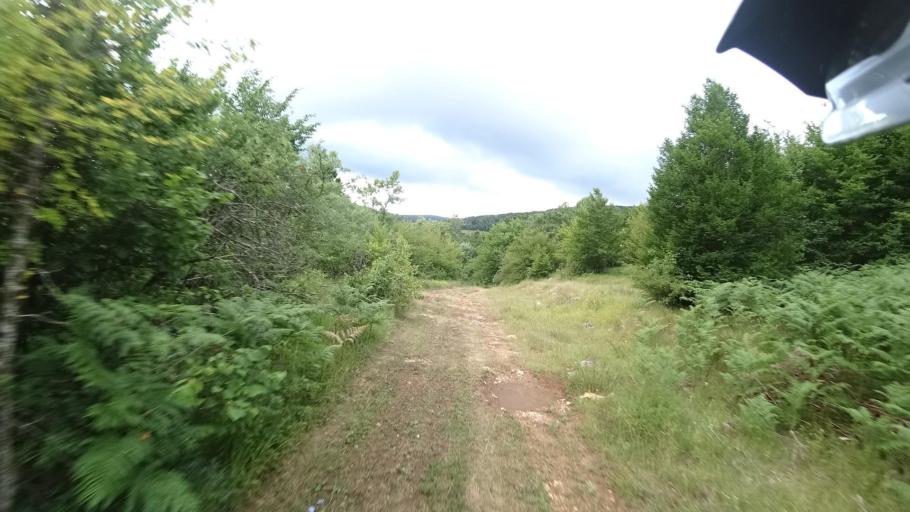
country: HR
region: Licko-Senjska
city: Jezerce
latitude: 44.7610
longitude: 15.4850
